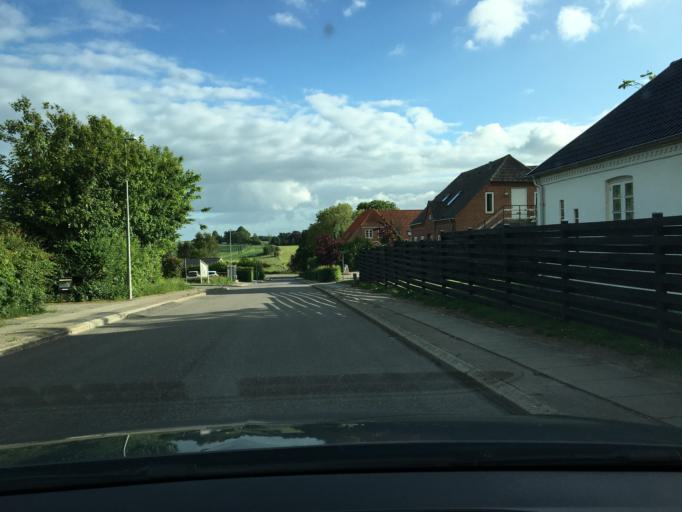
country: DK
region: Central Jutland
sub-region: Favrskov Kommune
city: Hadsten
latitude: 56.3094
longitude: 10.0946
